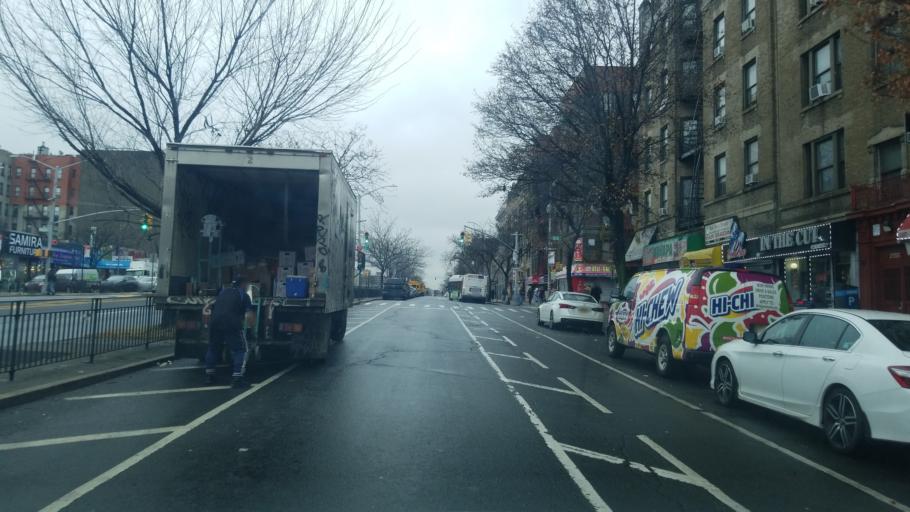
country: US
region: New York
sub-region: New York County
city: Inwood
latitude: 40.8592
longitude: -73.8991
